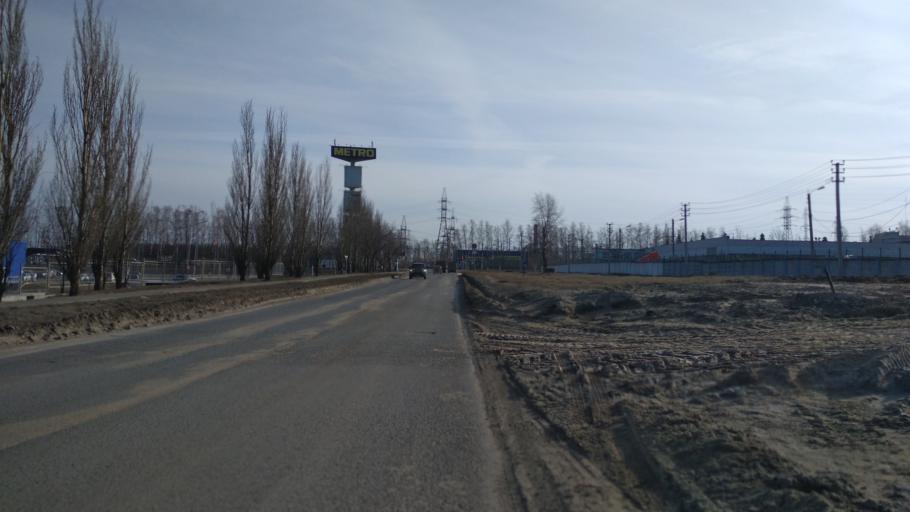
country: RU
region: Chuvashia
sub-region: Cheboksarskiy Rayon
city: Cheboksary
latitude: 56.1304
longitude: 47.3174
